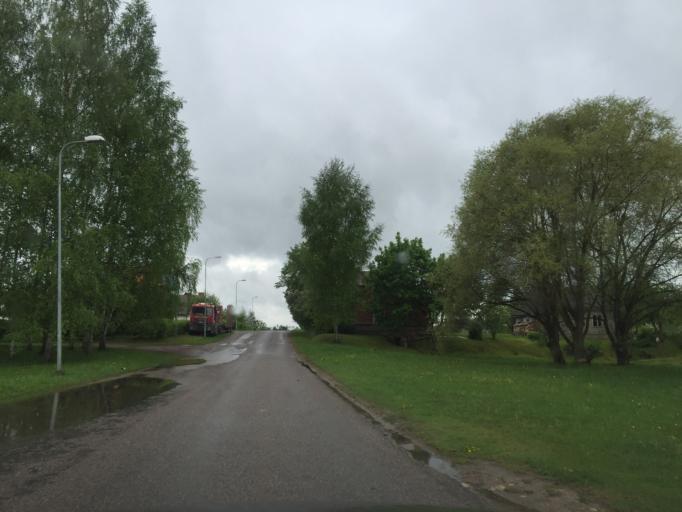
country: LV
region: Ogre
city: Jumprava
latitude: 56.6732
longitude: 24.9687
